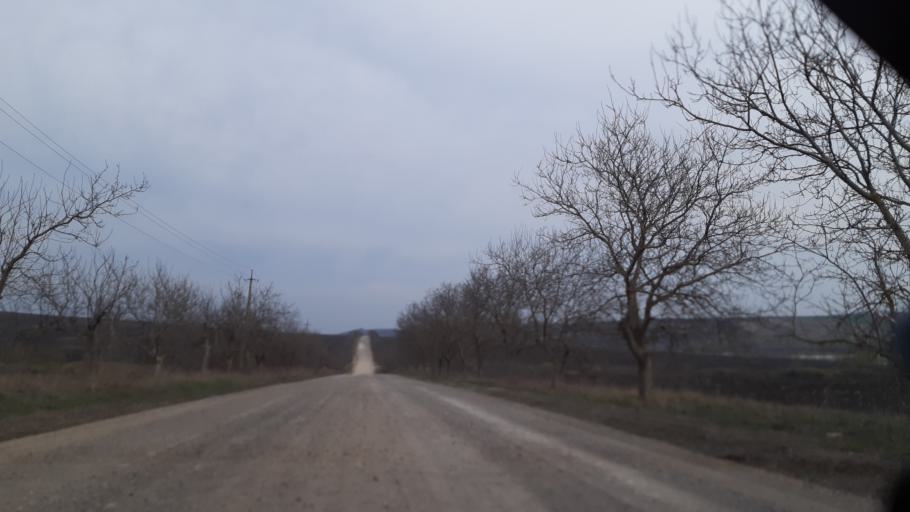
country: MD
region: Soldanesti
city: Soldanesti
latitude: 47.6990
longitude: 28.7257
